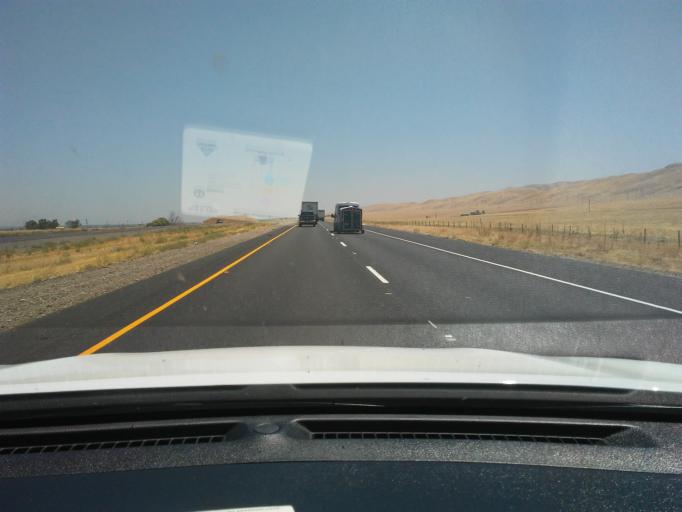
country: US
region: California
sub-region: San Joaquin County
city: Tracy
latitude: 37.6068
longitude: -121.3544
